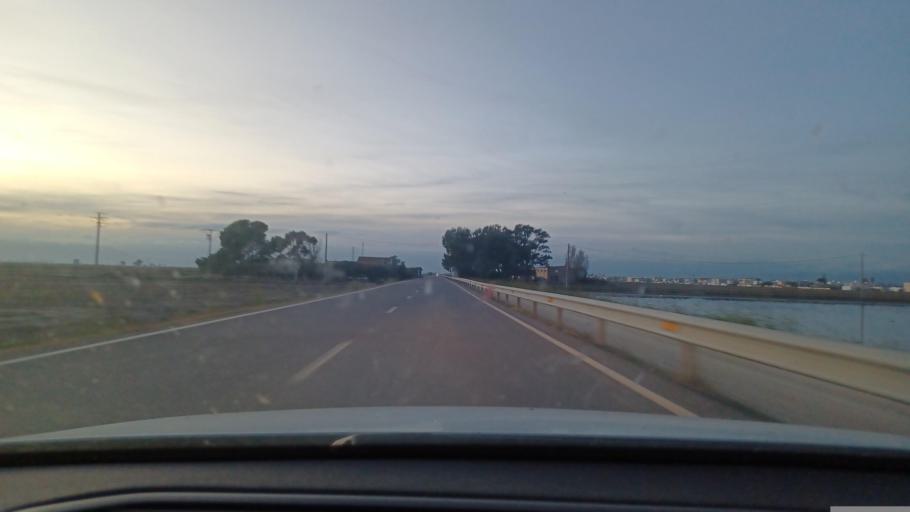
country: ES
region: Catalonia
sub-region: Provincia de Tarragona
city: Deltebre
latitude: 40.6629
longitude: 0.7626
